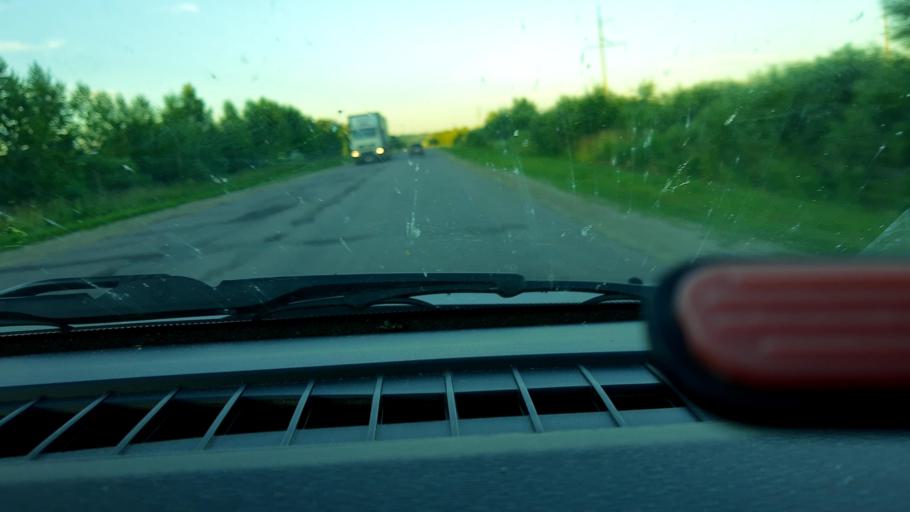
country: RU
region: Nizjnij Novgorod
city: Uren'
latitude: 57.5018
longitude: 45.8230
